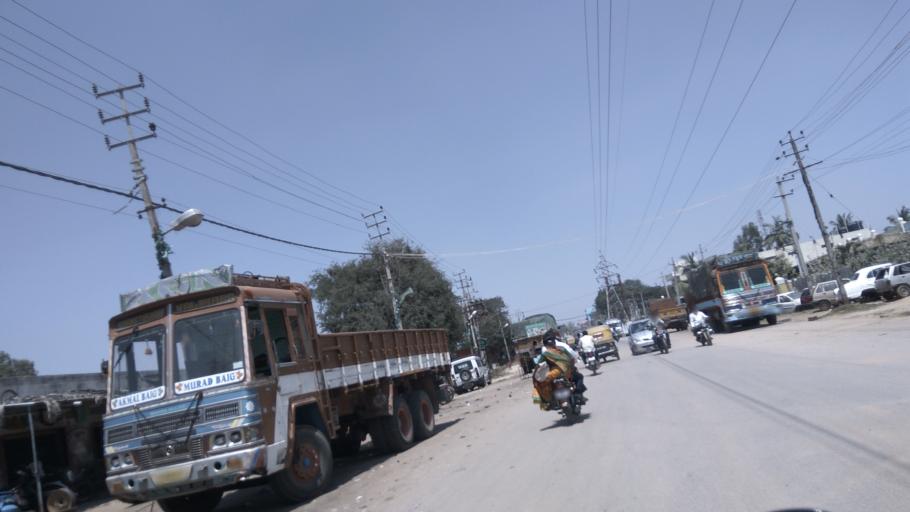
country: IN
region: Karnataka
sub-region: Kolar
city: Mulbagal
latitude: 13.1574
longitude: 78.3914
